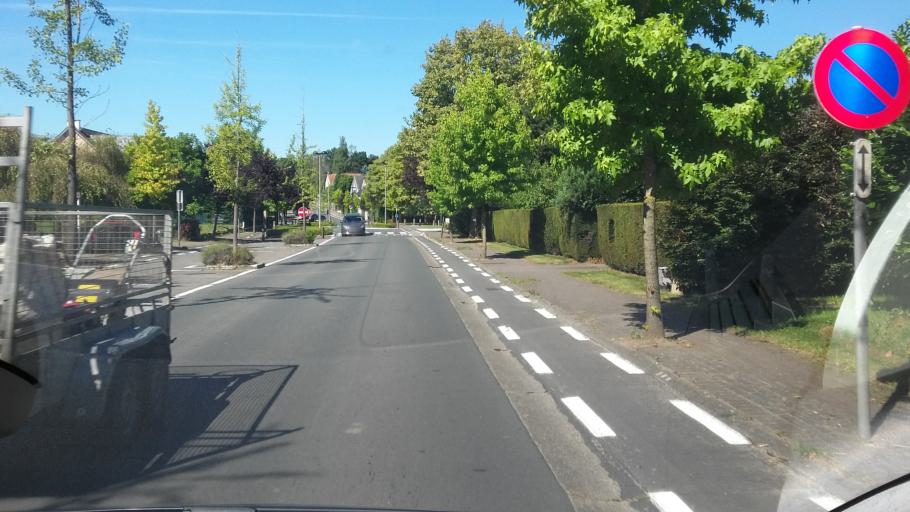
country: BE
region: Wallonia
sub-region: Province du Brabant Wallon
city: Waterloo
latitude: 50.7028
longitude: 4.4205
